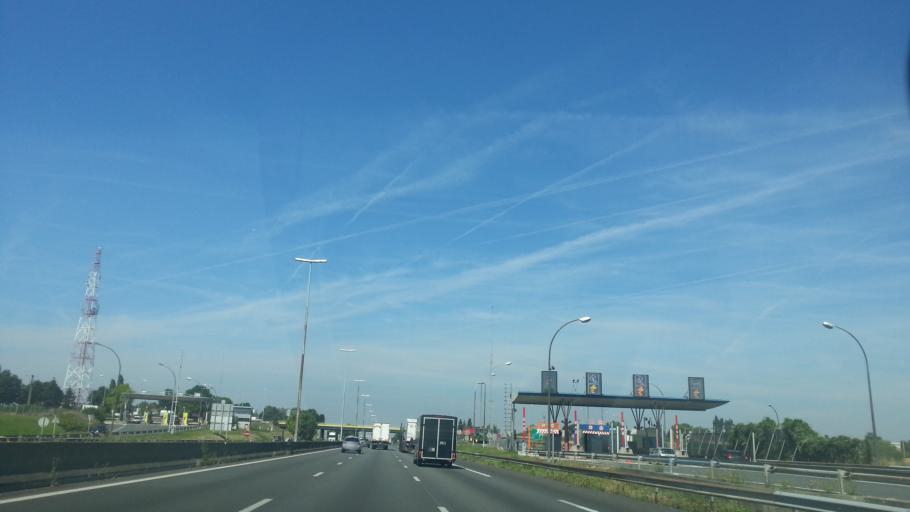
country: FR
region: Ile-de-France
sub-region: Departement du Val-d'Oise
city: Survilliers
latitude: 49.0835
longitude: 2.5513
